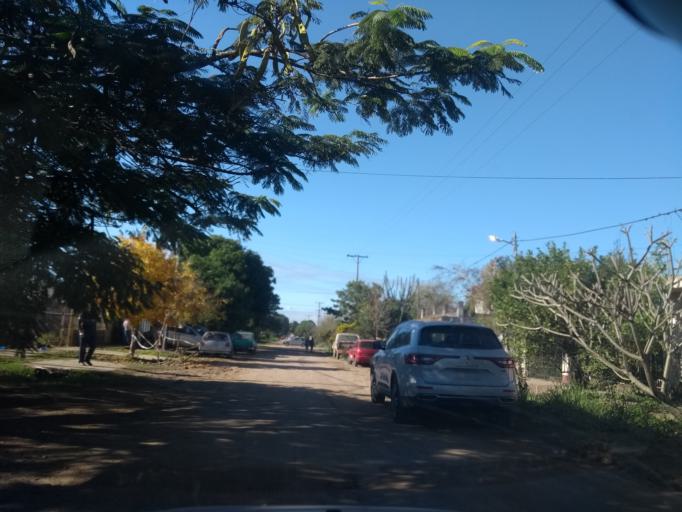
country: AR
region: Chaco
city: Barranqueras
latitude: -27.4791
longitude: -58.9313
